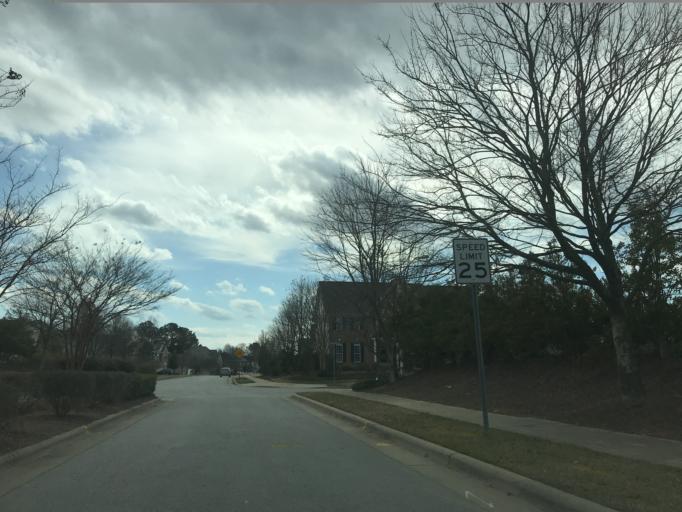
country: US
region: North Carolina
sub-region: Wake County
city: Green Level
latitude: 35.7841
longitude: -78.8563
